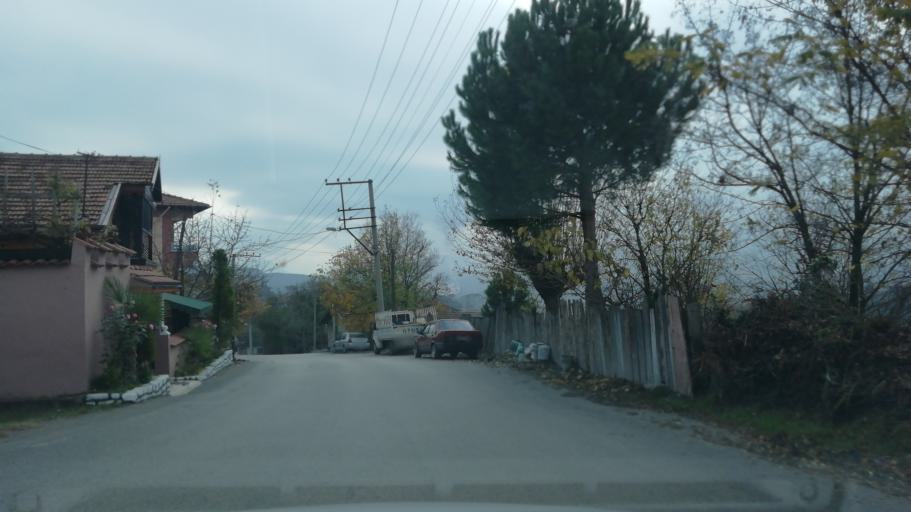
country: TR
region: Karabuk
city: Karabuk
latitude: 41.2187
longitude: 32.6276
